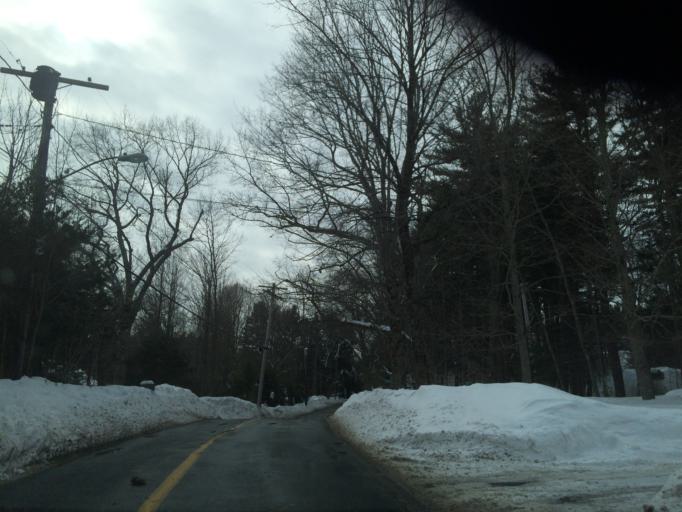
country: US
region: Massachusetts
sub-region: Middlesex County
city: Weston
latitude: 42.3923
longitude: -71.3215
